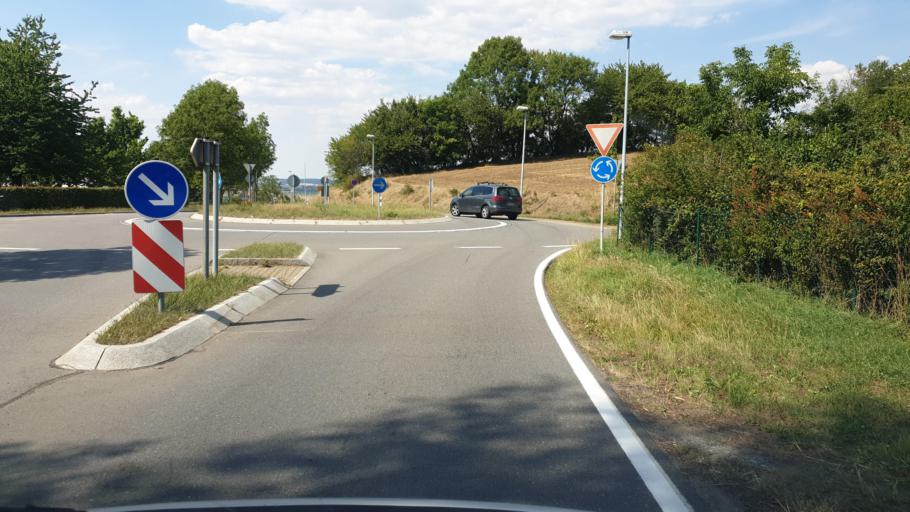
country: DE
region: Saxony
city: Zschopau
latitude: 50.7336
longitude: 13.0823
